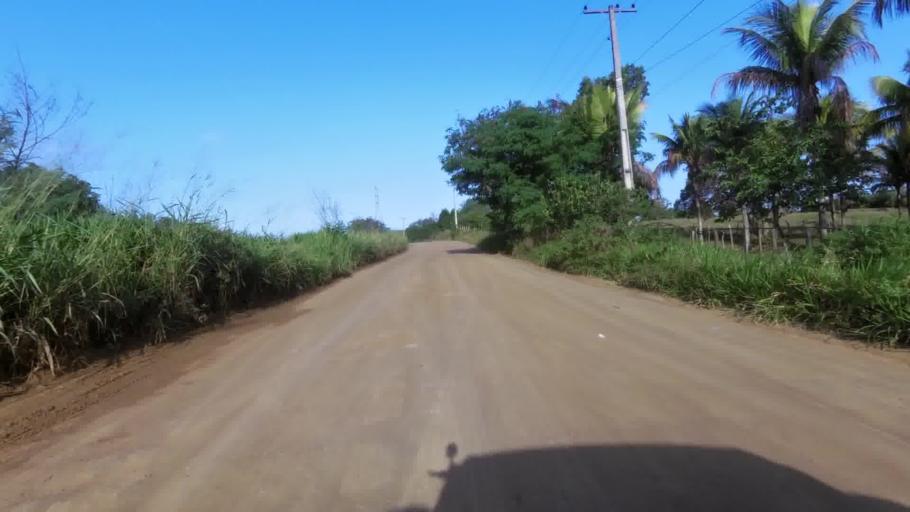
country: BR
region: Espirito Santo
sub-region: Guarapari
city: Guarapari
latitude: -20.7252
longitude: -40.5702
